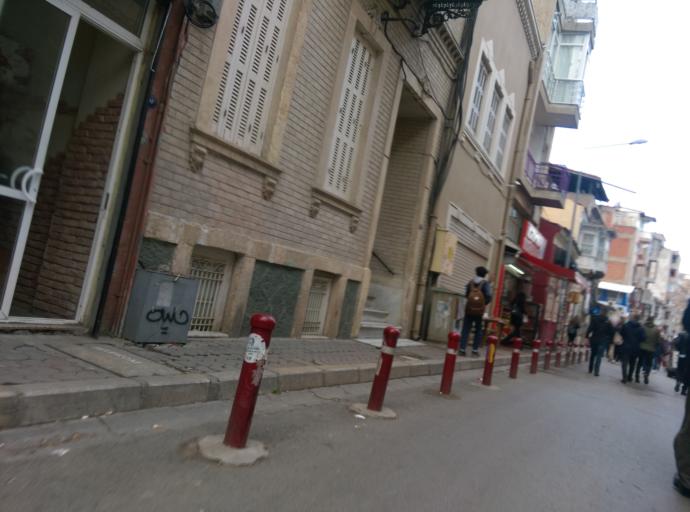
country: TR
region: Izmir
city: Izmir
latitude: 38.4391
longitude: 27.1463
